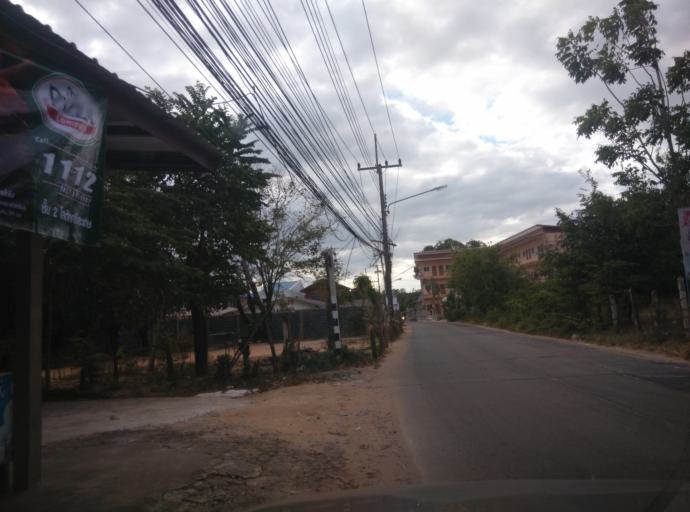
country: TH
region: Sisaket
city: Si Sa Ket
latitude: 15.1151
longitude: 104.3555
